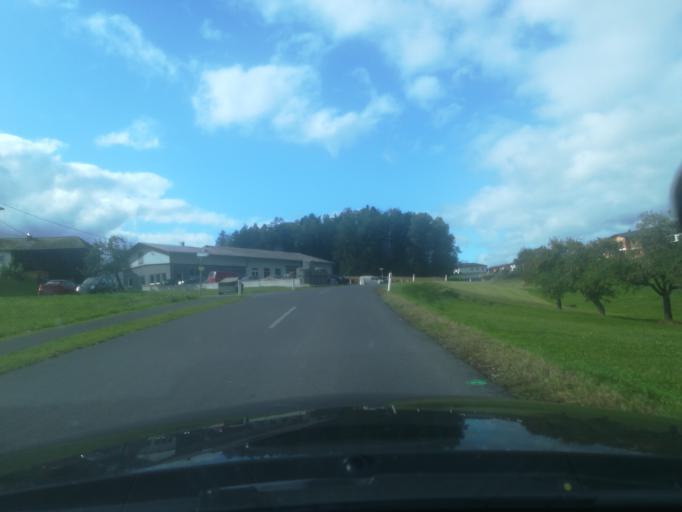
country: AT
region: Upper Austria
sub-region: Politischer Bezirk Urfahr-Umgebung
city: Herzogsdorf
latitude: 48.4303
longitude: 14.1221
